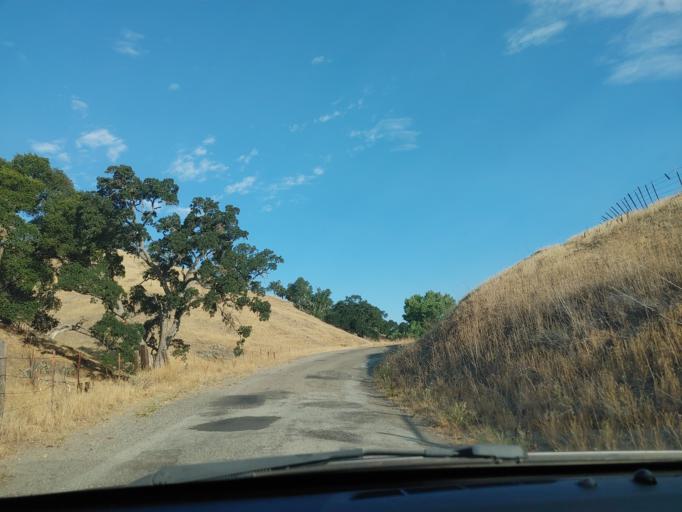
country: US
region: California
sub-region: San Benito County
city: Ridgemark
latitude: 36.7516
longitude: -121.1602
